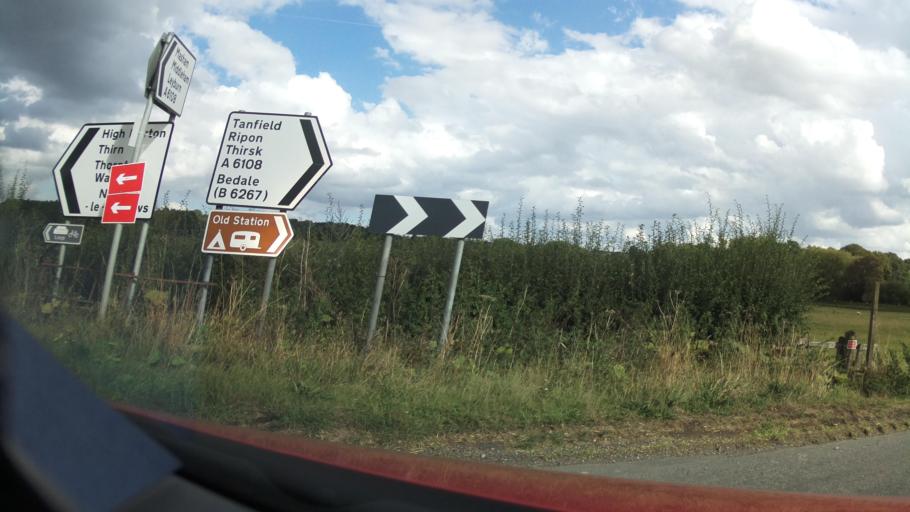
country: GB
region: England
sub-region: North Yorkshire
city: Bedale
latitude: 54.2262
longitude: -1.6542
